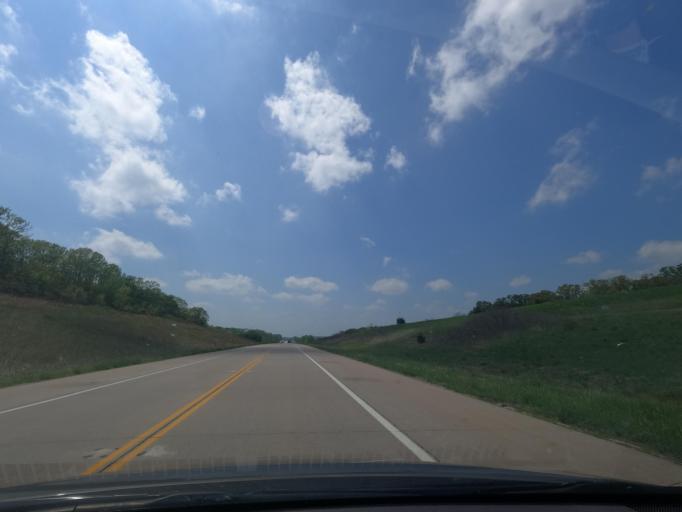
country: US
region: Kansas
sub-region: Wilson County
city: Fredonia
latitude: 37.6177
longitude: -95.9566
